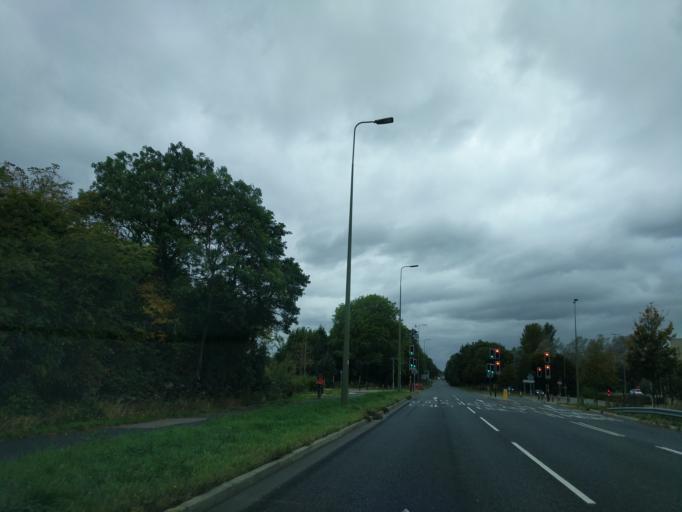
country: GB
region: England
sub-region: Oxfordshire
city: Cowley
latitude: 51.7706
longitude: -1.2180
